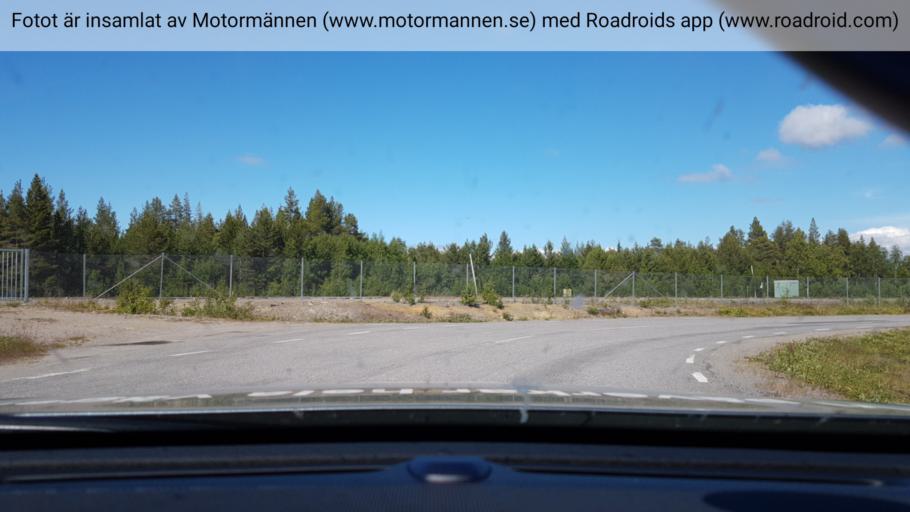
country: SE
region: Norrbotten
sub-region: Arjeplogs Kommun
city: Arjeplog
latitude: 65.5849
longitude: 18.1540
